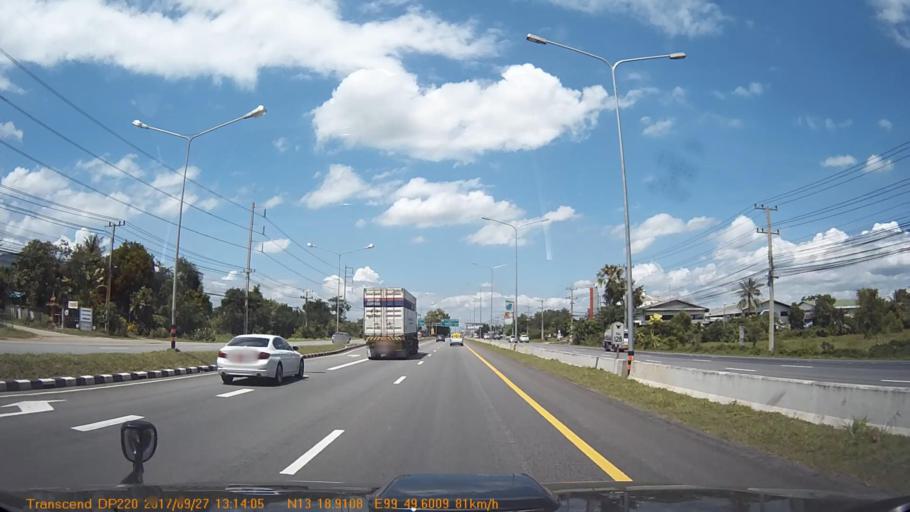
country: TH
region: Ratchaburi
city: Pak Tho
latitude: 13.3155
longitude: 99.8268
